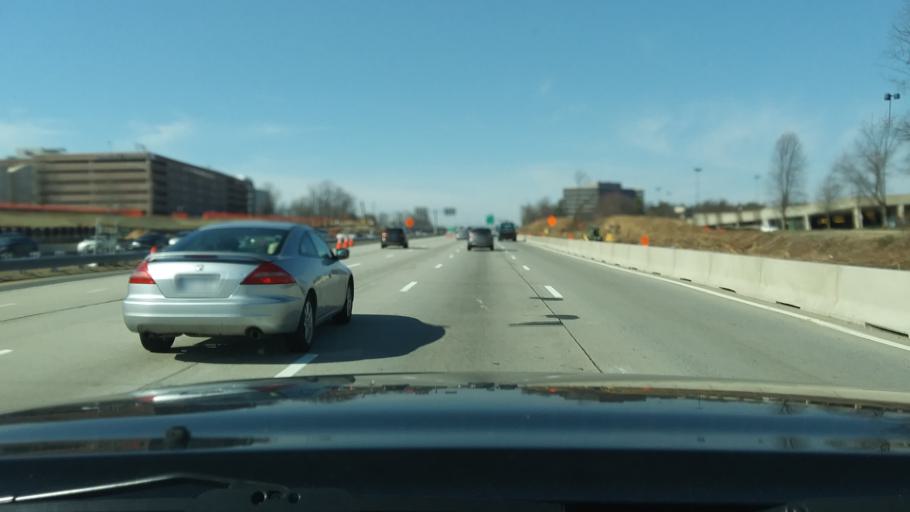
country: US
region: Virginia
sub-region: Fairfax County
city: Greenbriar
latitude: 38.8614
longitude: -77.3541
